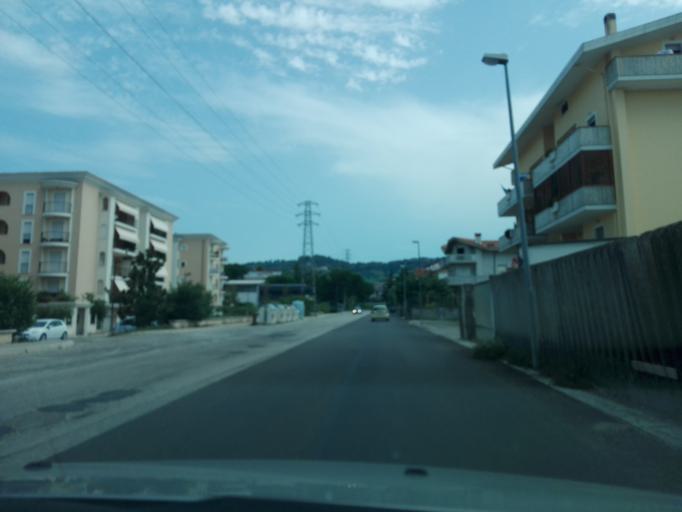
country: IT
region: Abruzzo
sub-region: Provincia di Pescara
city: Montesilvano Marina
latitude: 42.5051
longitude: 14.1322
